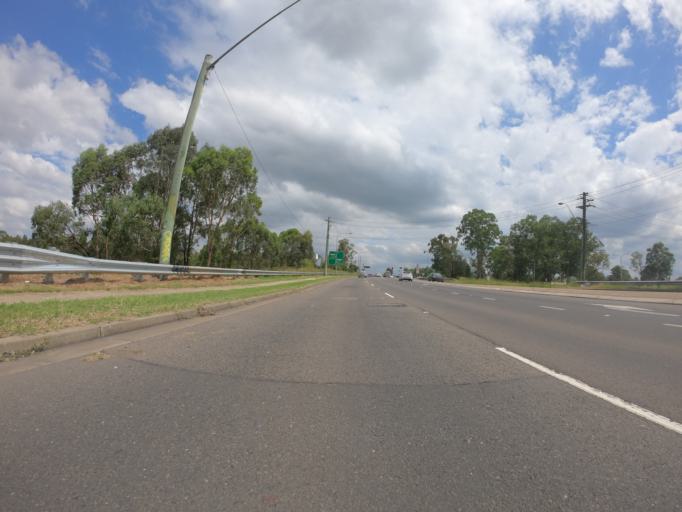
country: AU
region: New South Wales
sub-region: Blacktown
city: Mount Druitt
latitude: -33.7818
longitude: 150.7716
